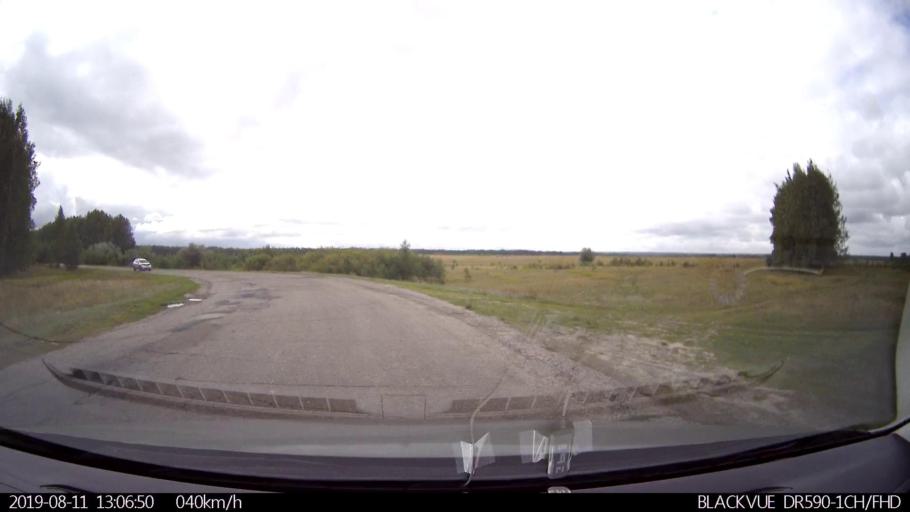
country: RU
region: Ulyanovsk
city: Ignatovka
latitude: 53.8668
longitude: 47.6398
